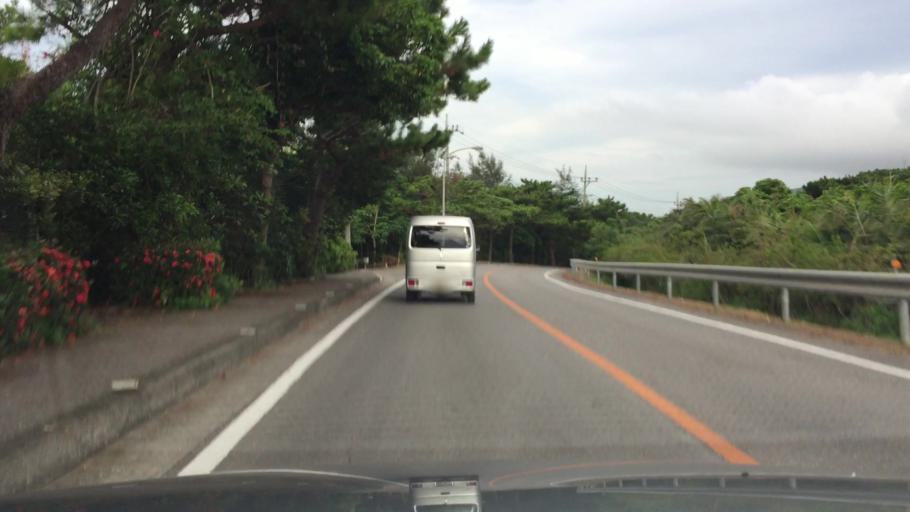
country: JP
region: Okinawa
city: Ishigaki
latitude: 24.4054
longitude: 124.1458
